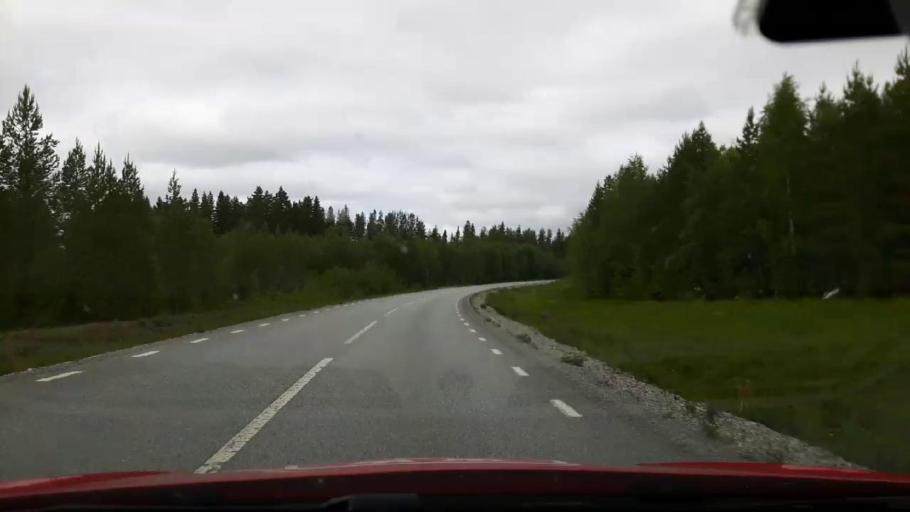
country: SE
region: Jaemtland
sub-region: OEstersunds Kommun
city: Lit
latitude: 63.6846
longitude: 14.6722
